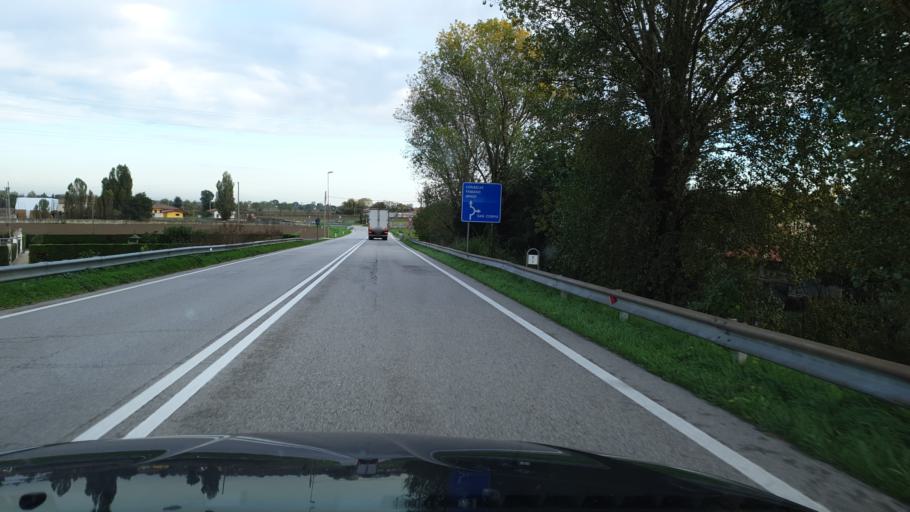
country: IT
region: Veneto
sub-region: Provincia di Padova
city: Monselice
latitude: 45.2336
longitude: 11.7764
